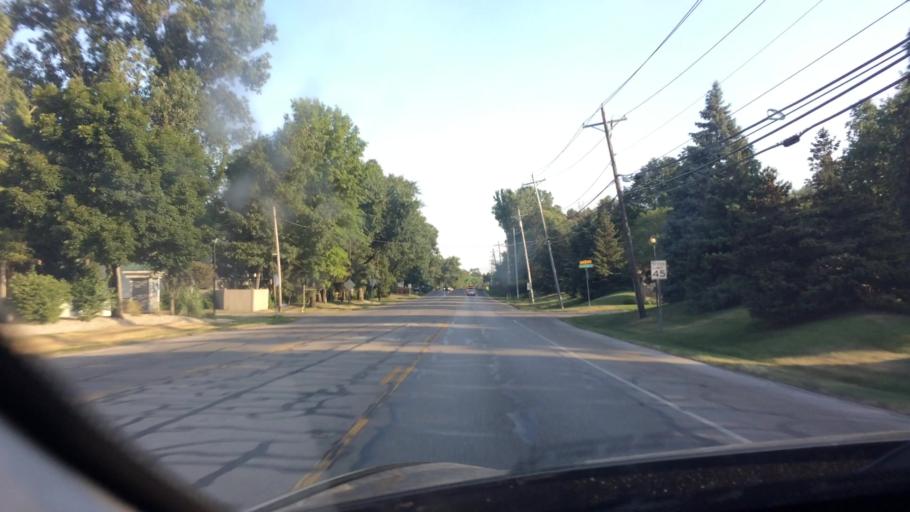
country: US
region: Ohio
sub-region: Lucas County
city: Holland
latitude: 41.6639
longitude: -83.7025
